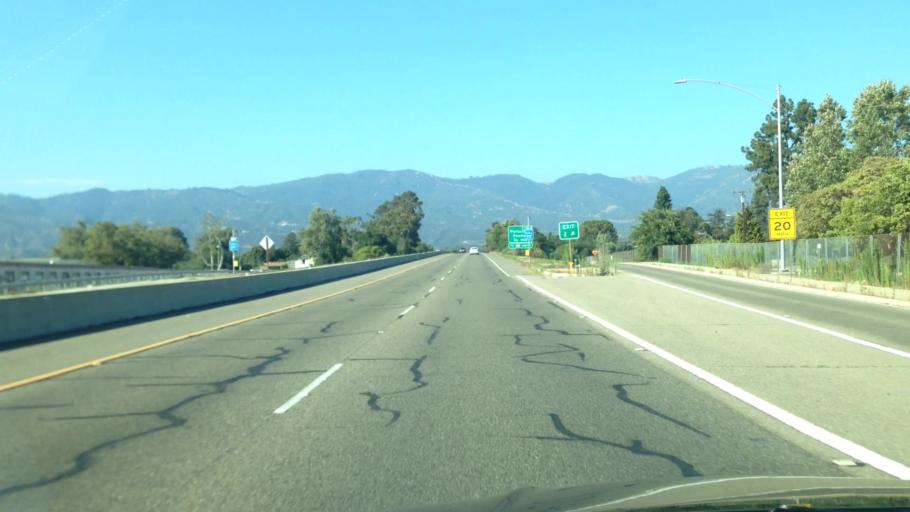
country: US
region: California
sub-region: Santa Barbara County
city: Goleta
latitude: 34.4321
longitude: -119.8204
